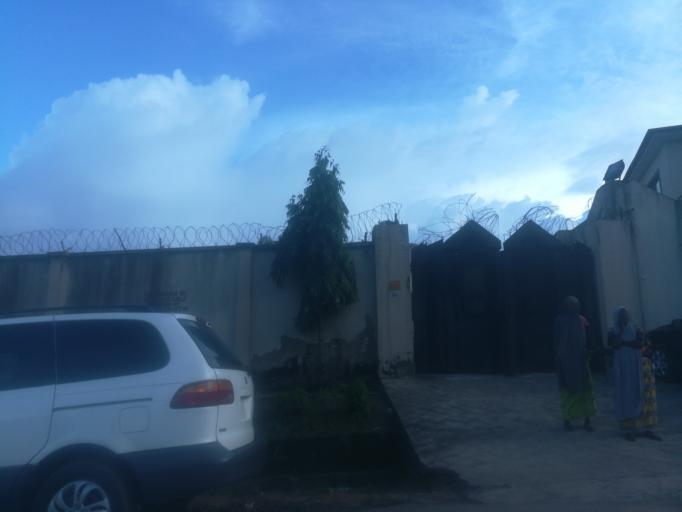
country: NG
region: Lagos
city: Ikeja
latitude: 6.6266
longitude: 3.3571
